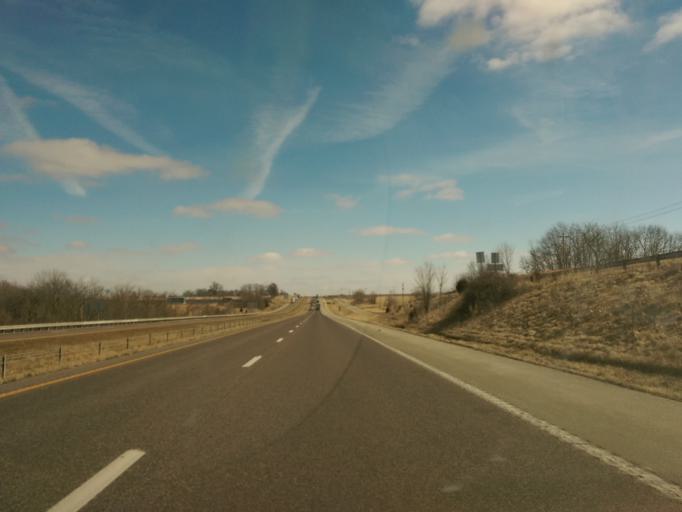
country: US
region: Missouri
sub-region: Callaway County
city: Fulton
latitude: 38.9441
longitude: -91.9297
